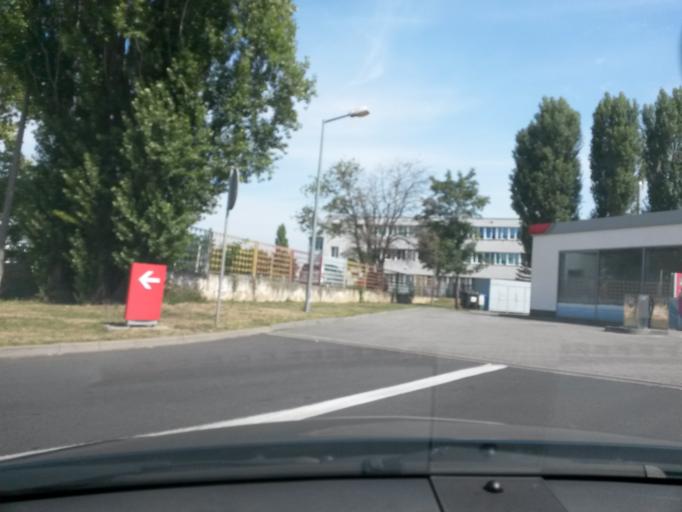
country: PL
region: Lower Silesian Voivodeship
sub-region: Powiat jaworski
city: Jawor
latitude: 51.0555
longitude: 16.2103
